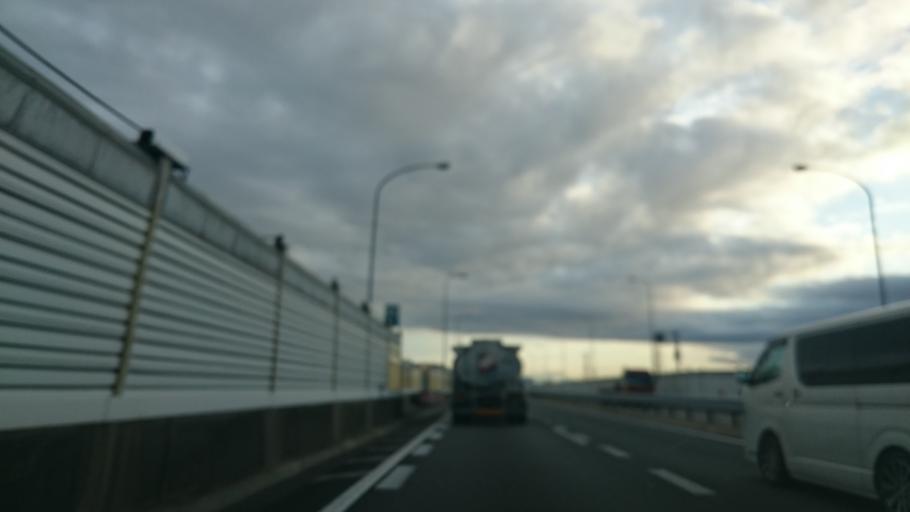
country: JP
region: Aichi
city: Nagoya-shi
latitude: 35.2262
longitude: 136.8922
